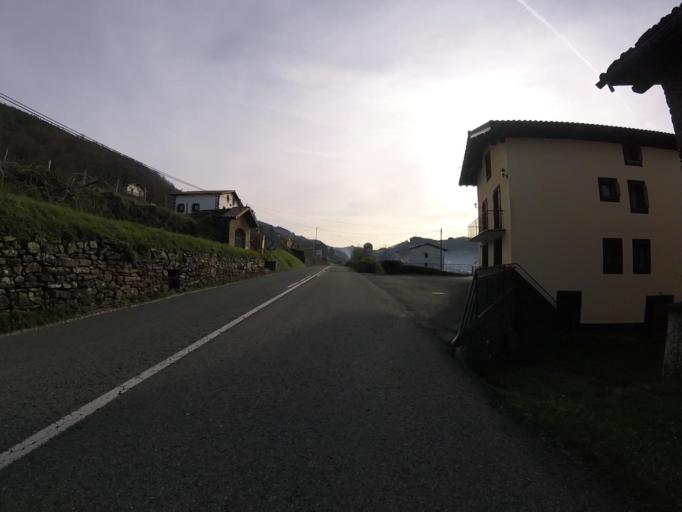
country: ES
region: Basque Country
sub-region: Provincia de Guipuzcoa
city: Berastegui
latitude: 43.1304
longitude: -1.9852
